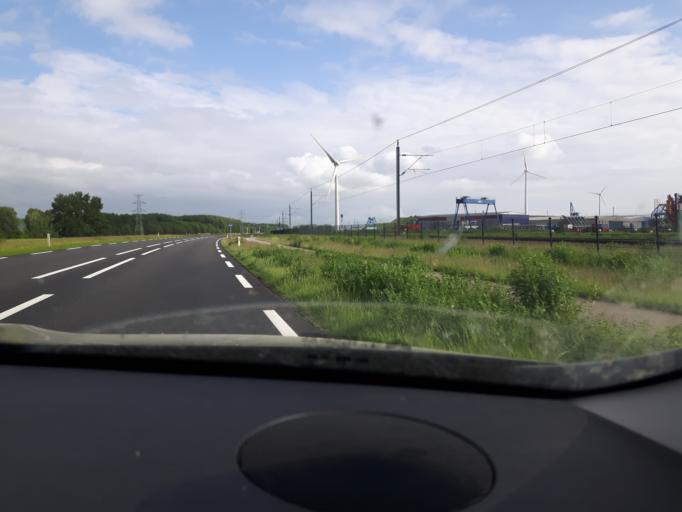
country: NL
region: Zeeland
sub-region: Gemeente Borsele
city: Borssele
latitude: 51.4752
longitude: 3.7207
